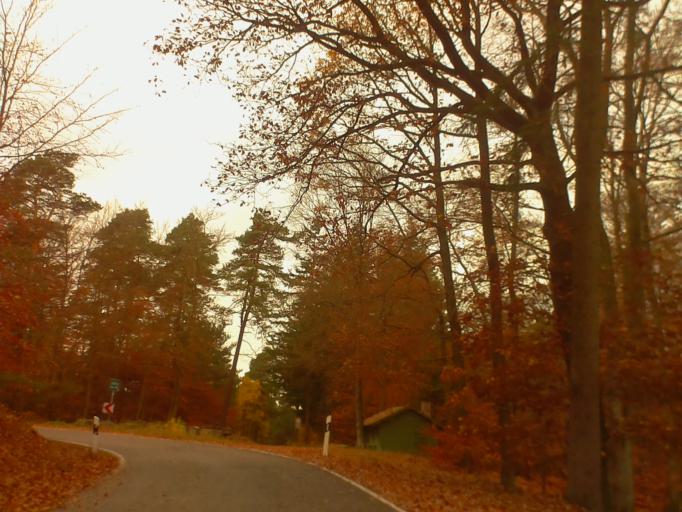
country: DE
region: Rheinland-Pfalz
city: Altleiningen
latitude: 49.4749
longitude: 8.0846
